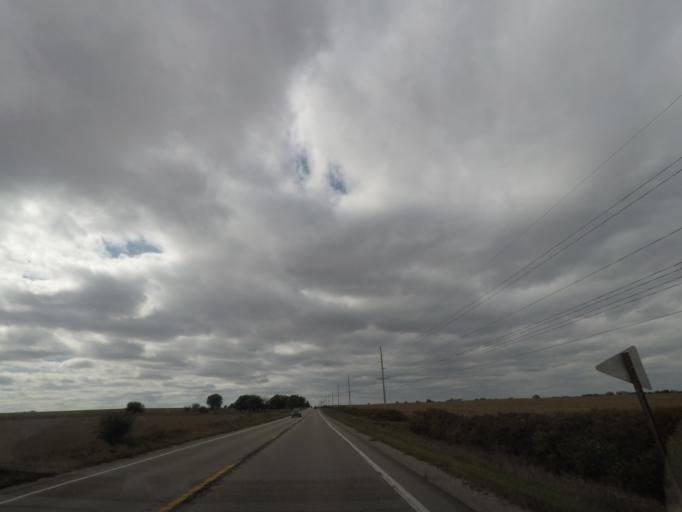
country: US
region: Iowa
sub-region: Story County
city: Huxley
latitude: 41.8778
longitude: -93.5435
